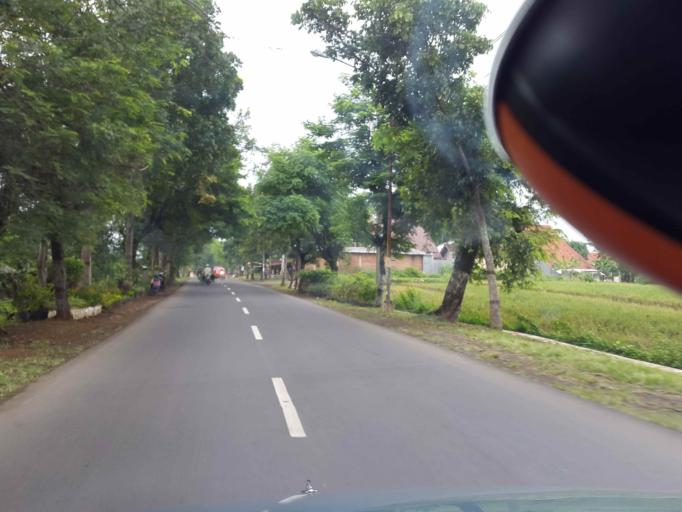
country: ID
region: Central Java
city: Wonopringgo
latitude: -7.0179
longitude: 109.6309
